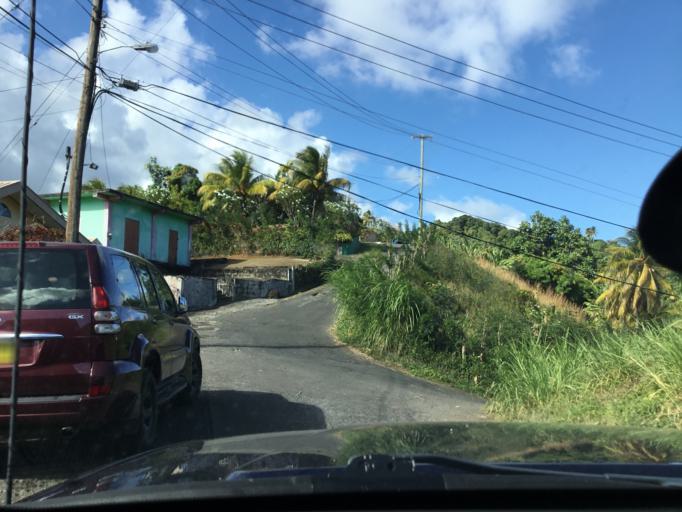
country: VC
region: Saint George
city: Kingstown
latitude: 13.1492
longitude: -61.1790
